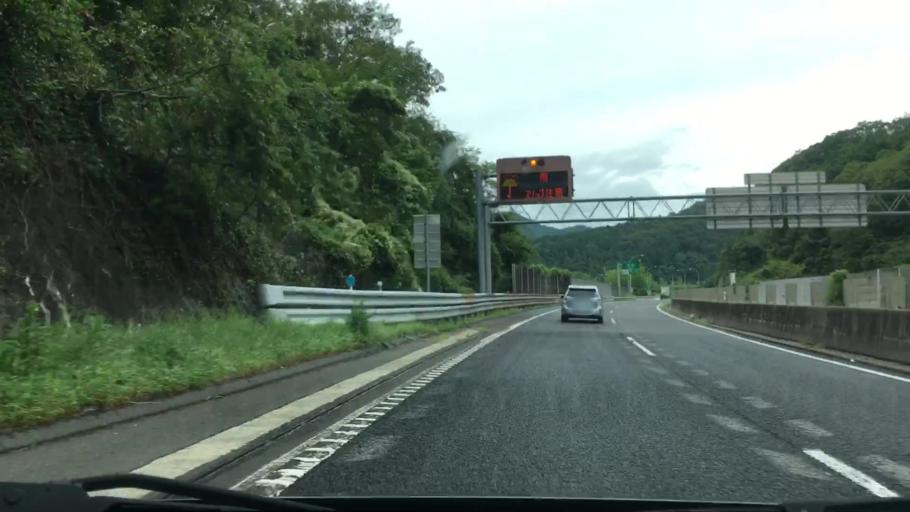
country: JP
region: Hyogo
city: Yamazakicho-nakabirose
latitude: 35.0202
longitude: 134.3757
